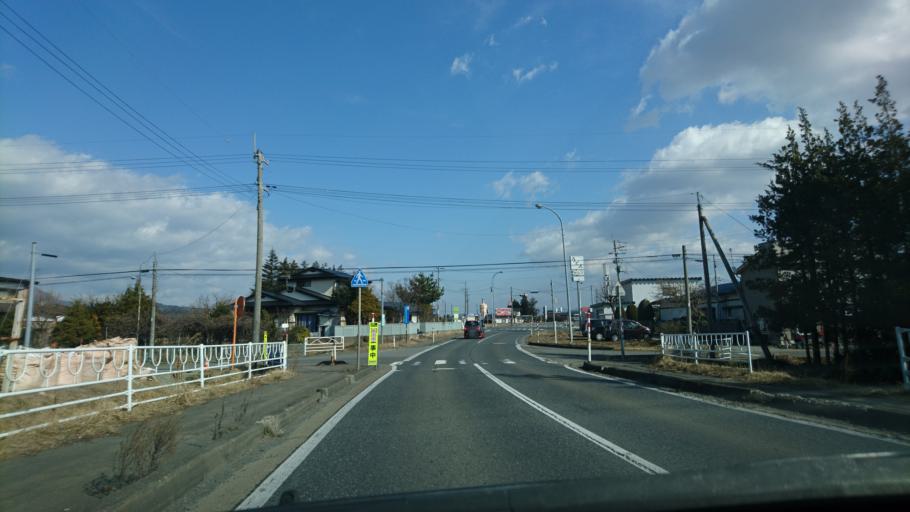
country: JP
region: Iwate
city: Morioka-shi
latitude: 39.5563
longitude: 141.1038
